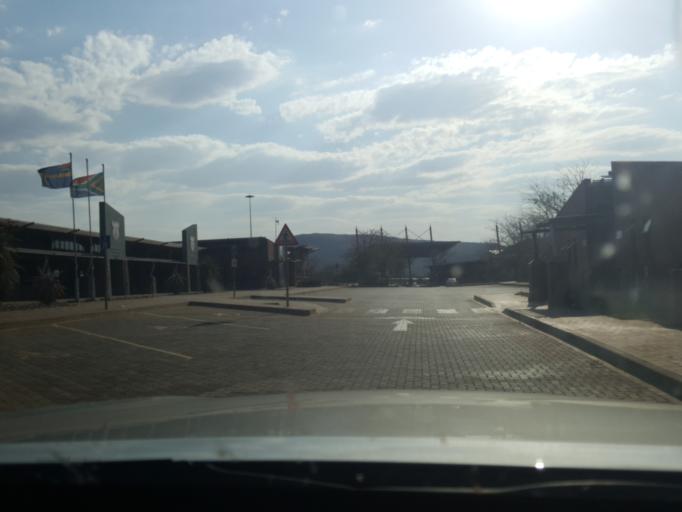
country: BW
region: South East
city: Lobatse
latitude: -25.2781
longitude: 25.7164
